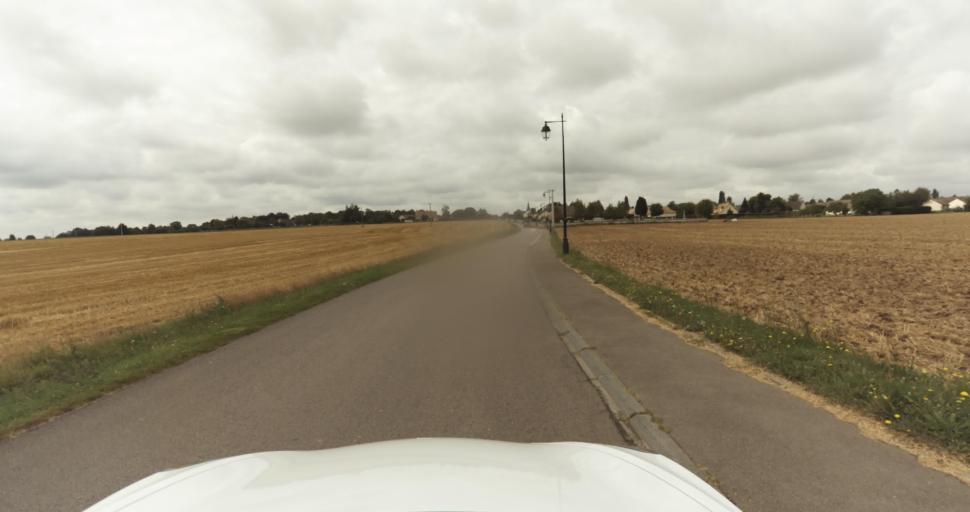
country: FR
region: Haute-Normandie
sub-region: Departement de l'Eure
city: Claville
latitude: 49.0266
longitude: 1.0412
